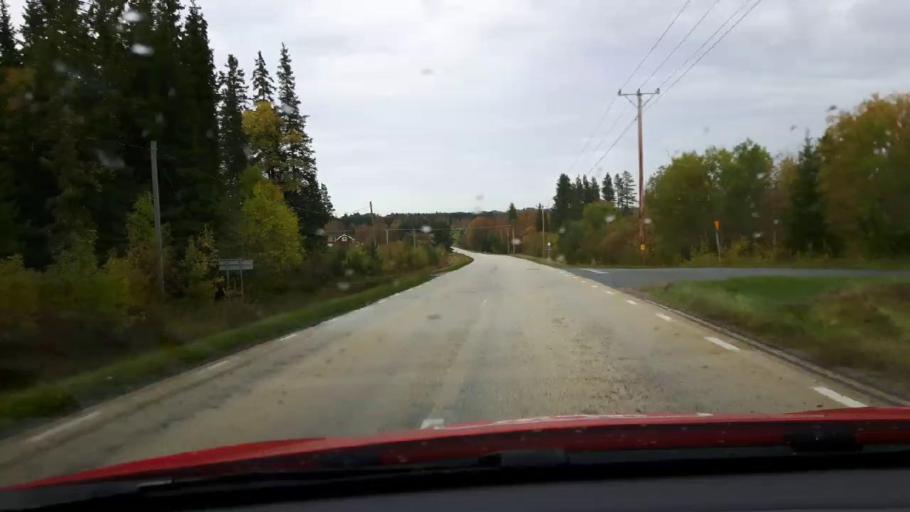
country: SE
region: Jaemtland
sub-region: Bergs Kommun
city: Hoverberg
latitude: 62.9721
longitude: 14.3489
